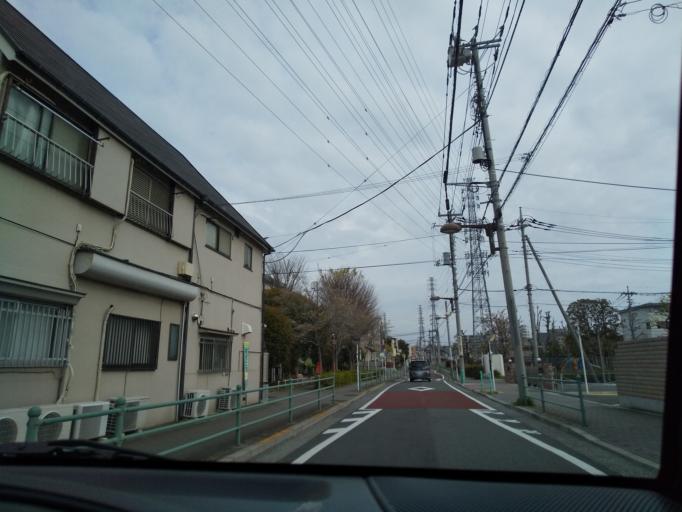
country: JP
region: Tokyo
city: Kokubunji
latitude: 35.6897
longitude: 139.4557
